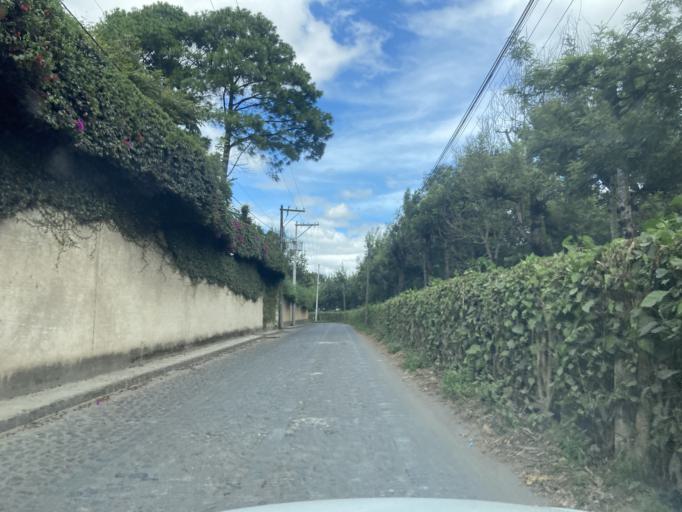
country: GT
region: Sacatepequez
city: Antigua Guatemala
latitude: 14.5475
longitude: -90.7337
